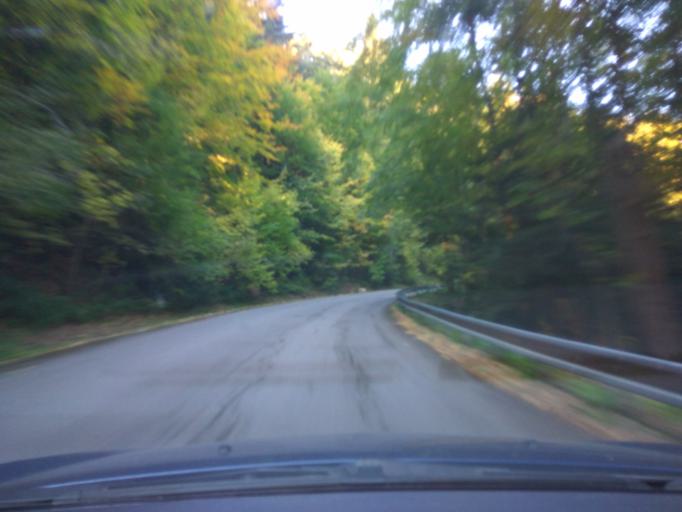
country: SK
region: Banskobystricky
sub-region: Okres Ziar nad Hronom
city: Kremnica
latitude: 48.7230
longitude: 18.9785
